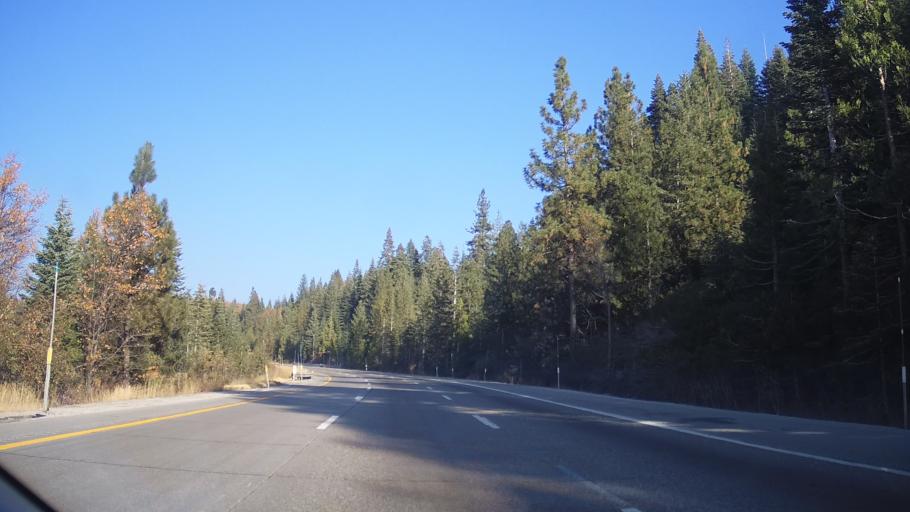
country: US
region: California
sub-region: Placer County
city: Foresthill
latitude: 39.2543
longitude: -120.7348
